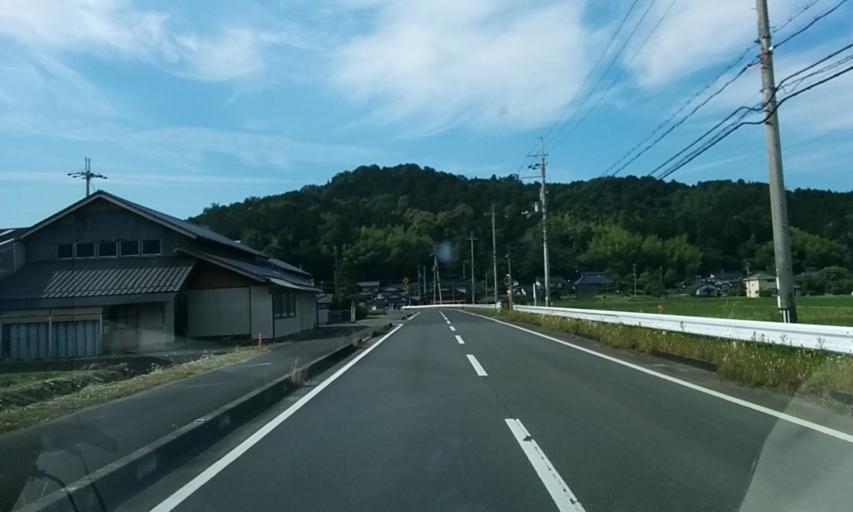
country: JP
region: Kyoto
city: Ayabe
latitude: 35.3296
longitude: 135.2079
